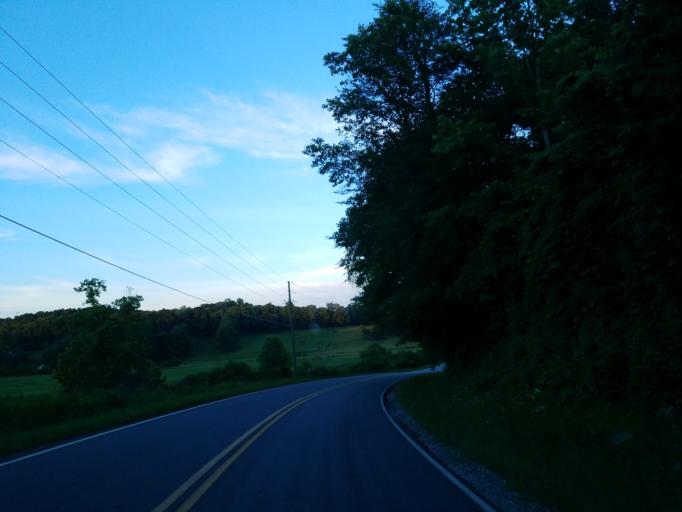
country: US
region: Georgia
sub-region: Lumpkin County
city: Dahlonega
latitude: 34.5661
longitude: -83.9618
